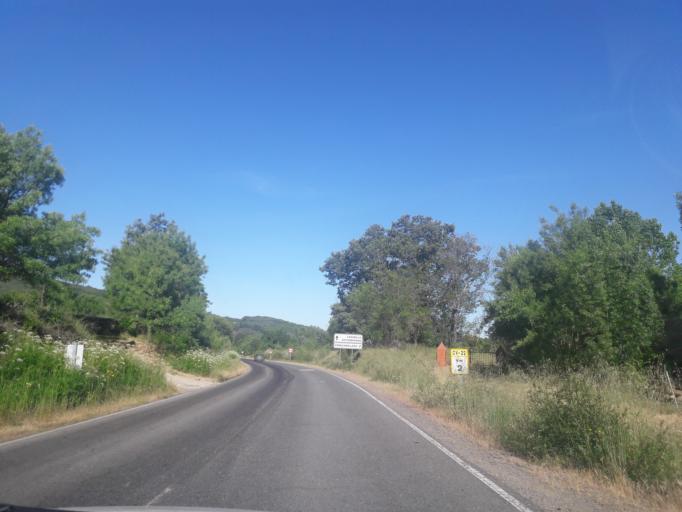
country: ES
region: Castille and Leon
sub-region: Provincia de Salamanca
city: Penacaballera
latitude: 40.3436
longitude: -5.8643
